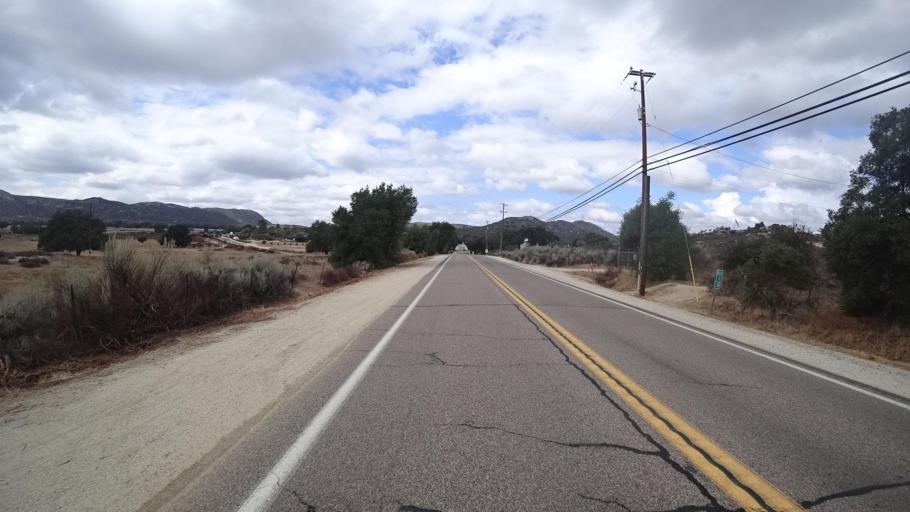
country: US
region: California
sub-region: San Diego County
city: Campo
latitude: 32.6402
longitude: -116.4819
